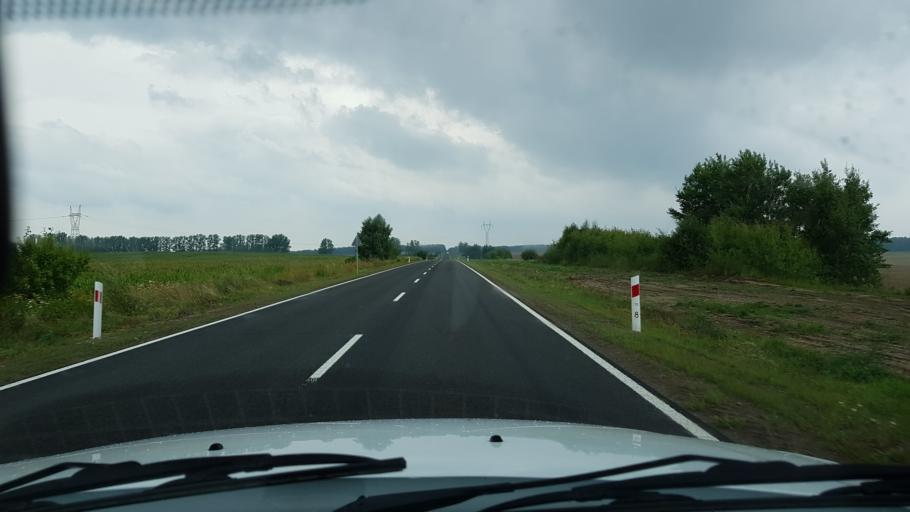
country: PL
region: West Pomeranian Voivodeship
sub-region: Powiat goleniowski
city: Maszewo
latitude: 53.4307
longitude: 14.9703
